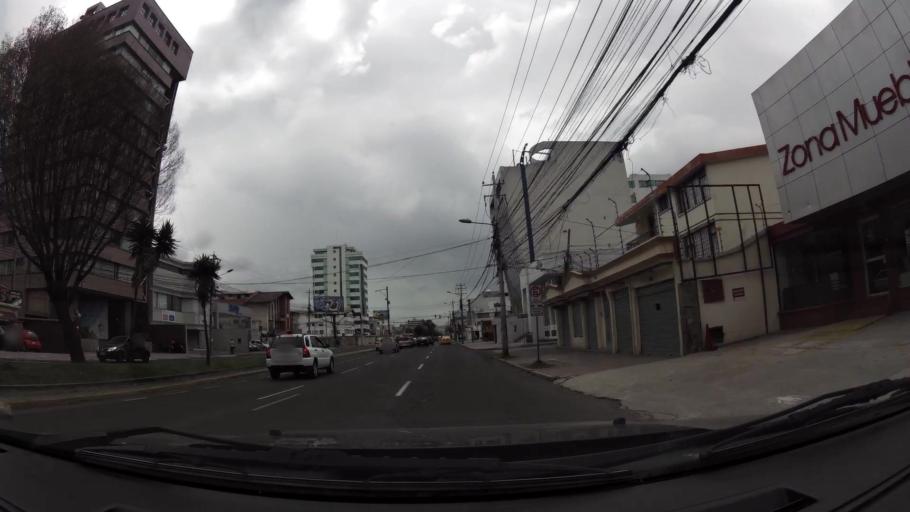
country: EC
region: Pichincha
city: Quito
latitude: -0.1738
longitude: -78.4804
